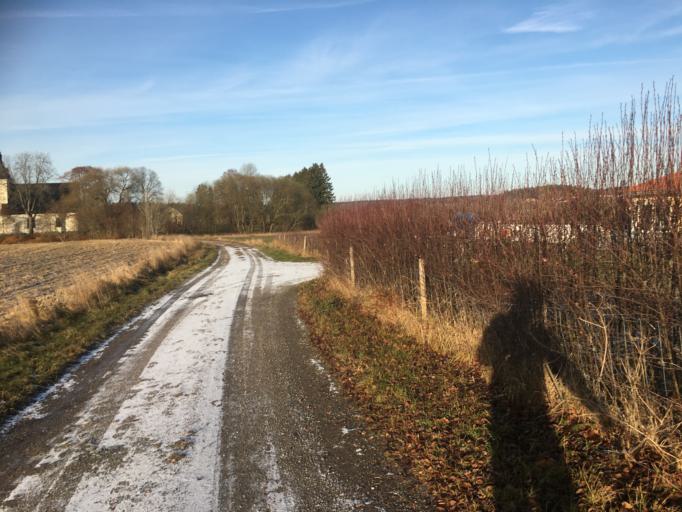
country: SE
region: Vaestmanland
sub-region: Vasteras
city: Vasteras
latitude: 59.6426
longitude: 16.4812
